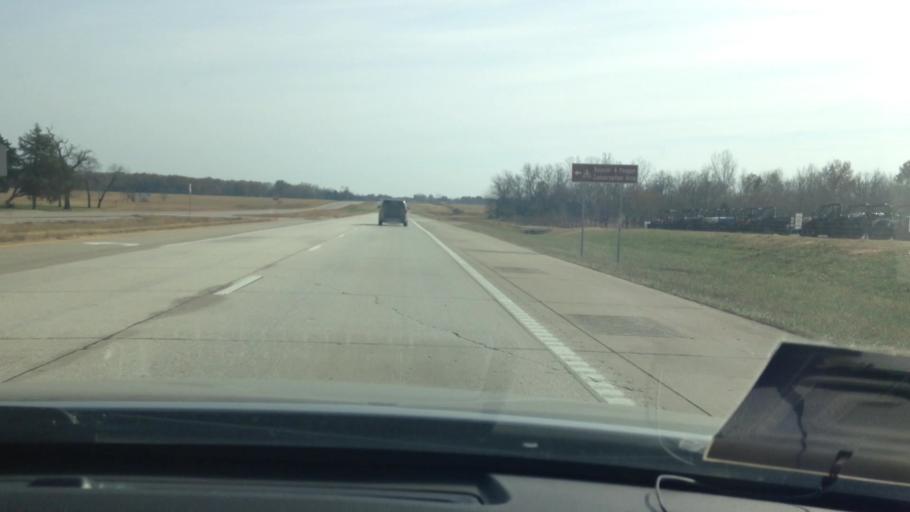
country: US
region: Missouri
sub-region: Henry County
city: Clinton
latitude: 38.4128
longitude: -93.8568
